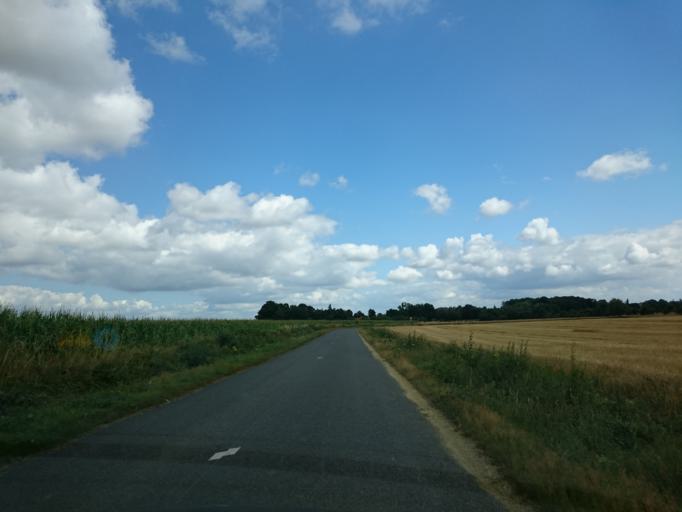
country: FR
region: Brittany
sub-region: Departement d'Ille-et-Vilaine
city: Chanteloup
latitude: 47.9537
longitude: -1.6410
